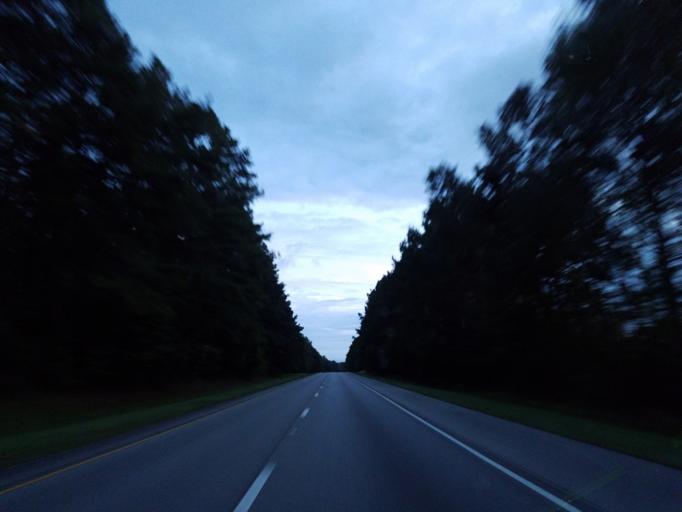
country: US
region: Mississippi
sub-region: Clarke County
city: Stonewall
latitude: 32.1477
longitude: -88.8692
